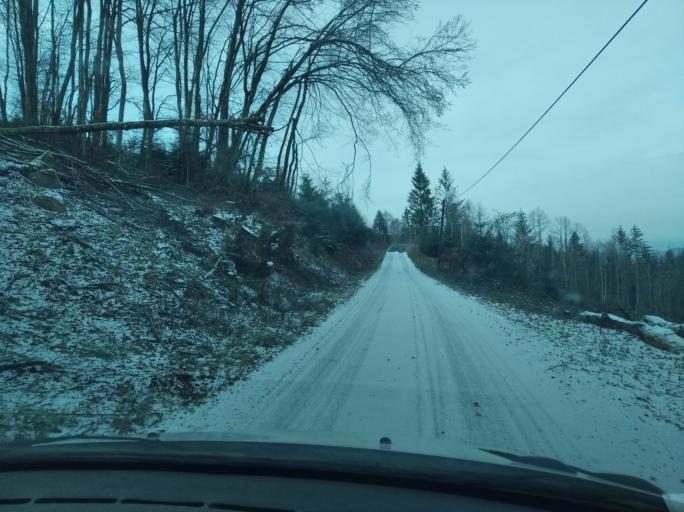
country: FR
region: Rhone-Alpes
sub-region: Departement de la Loire
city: La Pacaudiere
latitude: 46.1371
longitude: 3.7789
